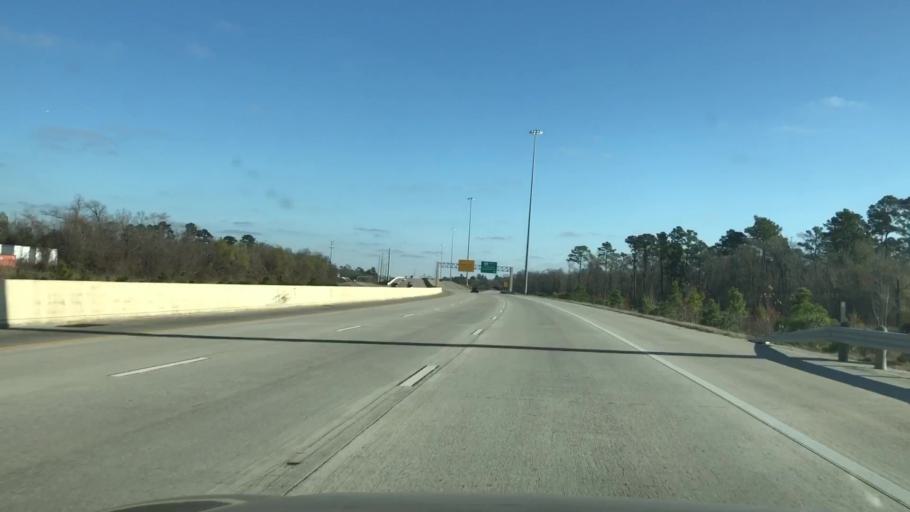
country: US
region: Texas
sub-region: Harris County
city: Jacinto City
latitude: 29.7962
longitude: -95.2267
